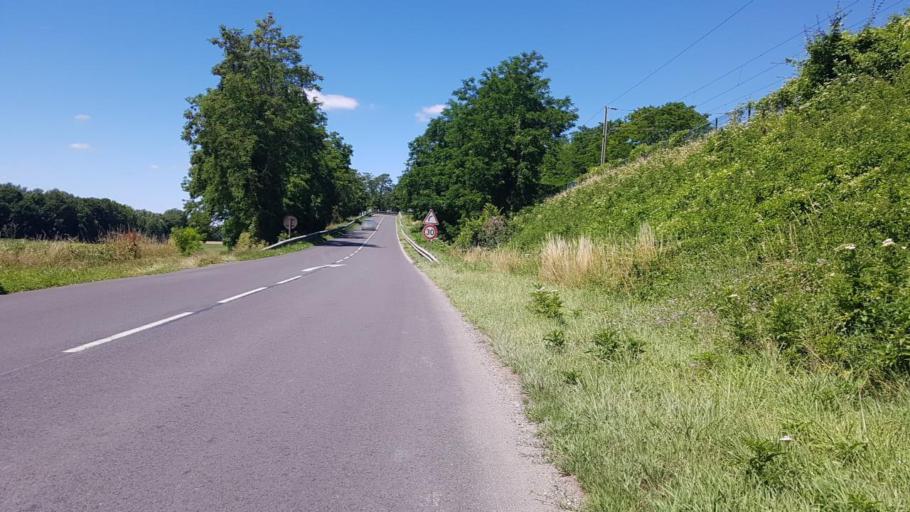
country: FR
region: Ile-de-France
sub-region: Departement de Seine-et-Marne
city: Sammeron
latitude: 48.9532
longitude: 3.0967
